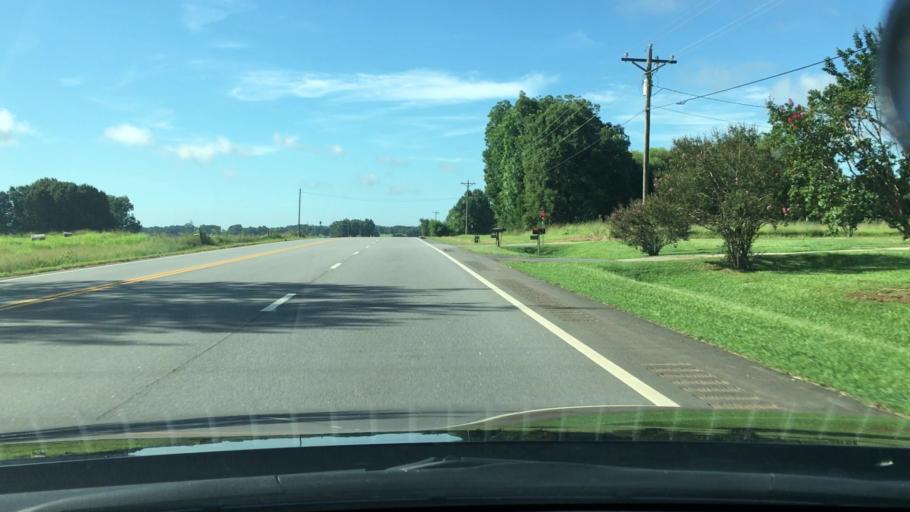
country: US
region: Georgia
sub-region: Morgan County
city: Madison
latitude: 33.4945
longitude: -83.4382
